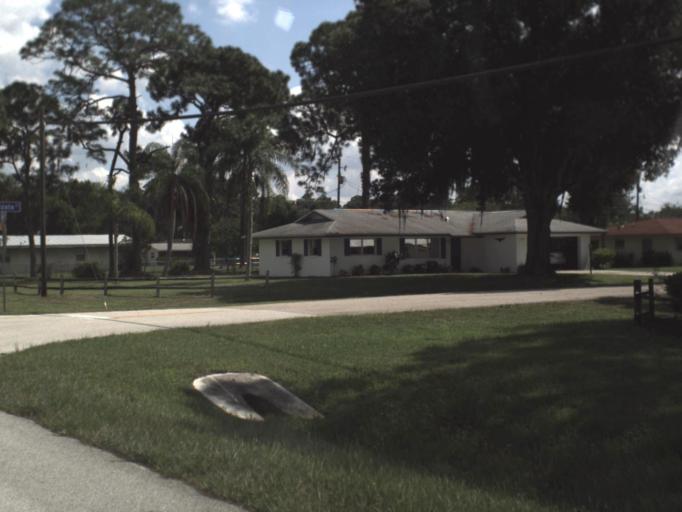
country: US
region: Florida
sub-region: Lee County
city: Fort Myers Shores
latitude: 26.7149
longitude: -81.7832
